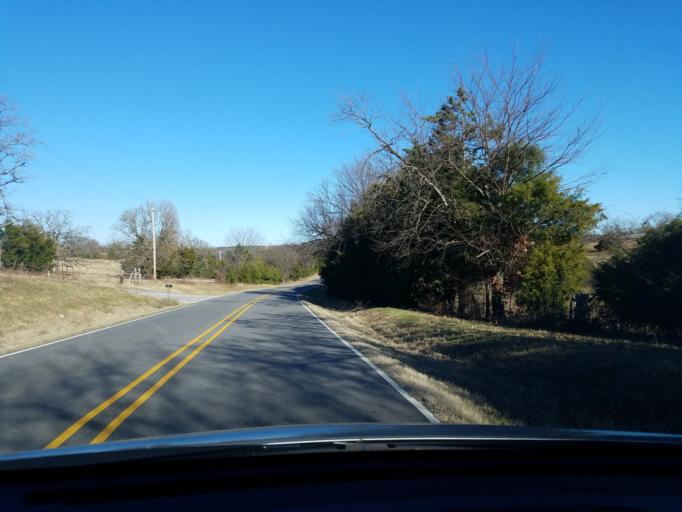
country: US
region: Arkansas
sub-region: Carroll County
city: Berryville
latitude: 36.3997
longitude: -93.5478
